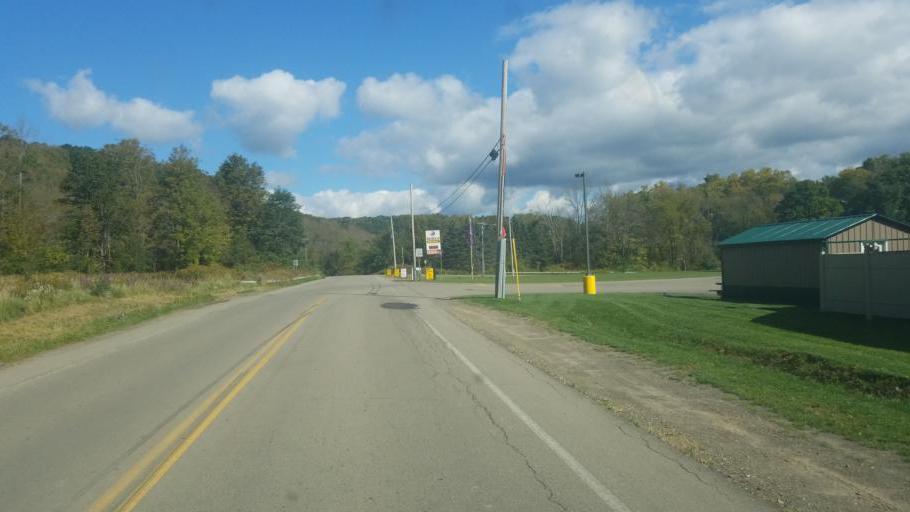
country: US
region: New York
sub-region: Allegany County
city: Cuba
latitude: 42.2359
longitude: -78.3109
